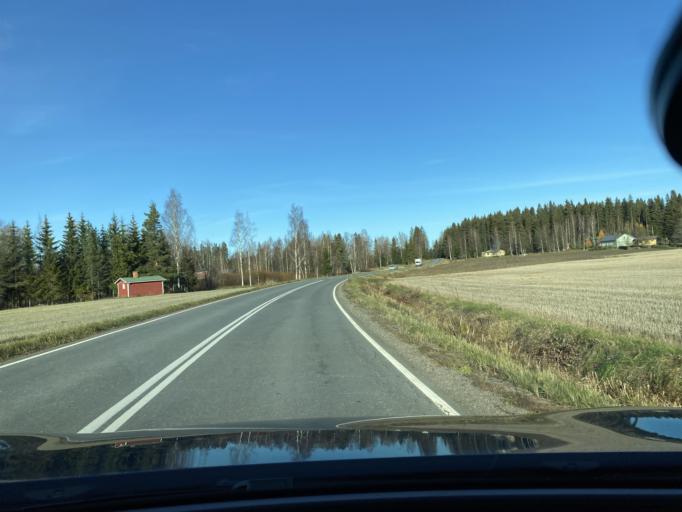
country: FI
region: Haeme
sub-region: Forssa
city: Tammela
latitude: 60.8414
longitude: 23.8335
